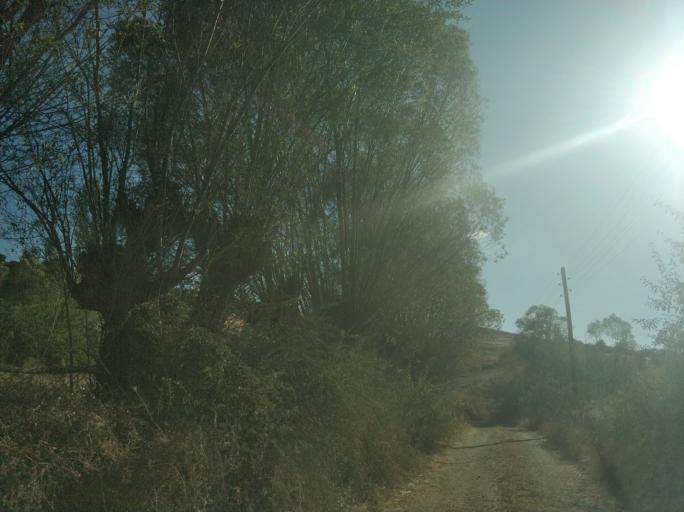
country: TR
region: Sivas
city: Zara
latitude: 39.8294
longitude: 37.9017
